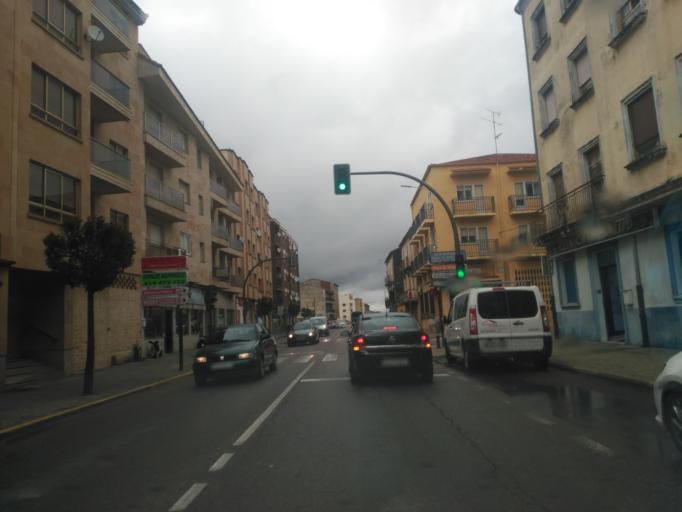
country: ES
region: Castille and Leon
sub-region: Provincia de Salamanca
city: Guijuelo
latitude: 40.5597
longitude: -5.6725
